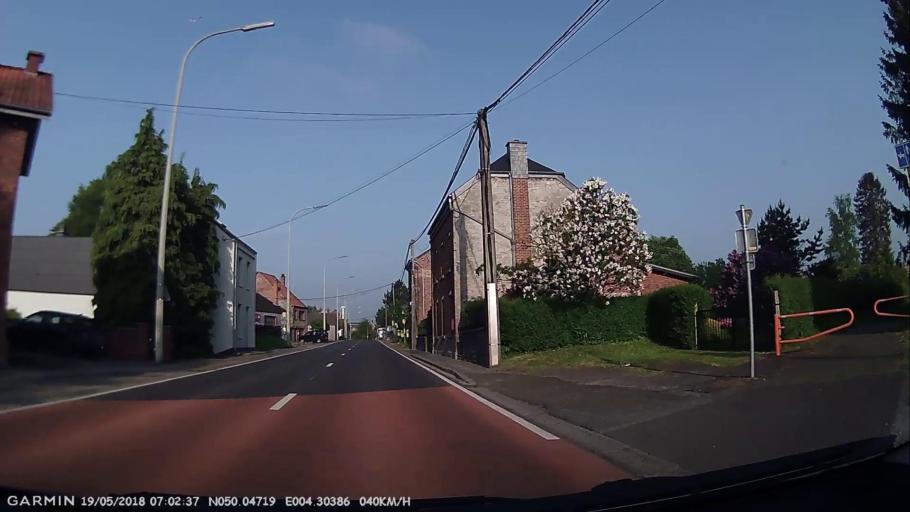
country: BE
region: Wallonia
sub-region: Province du Hainaut
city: Chimay
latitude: 50.0472
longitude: 4.3038
